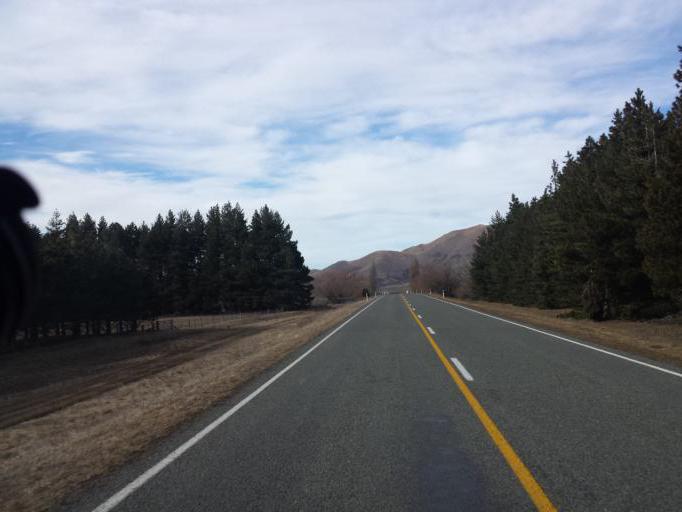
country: NZ
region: Canterbury
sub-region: Timaru District
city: Pleasant Point
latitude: -44.0869
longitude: 170.5445
